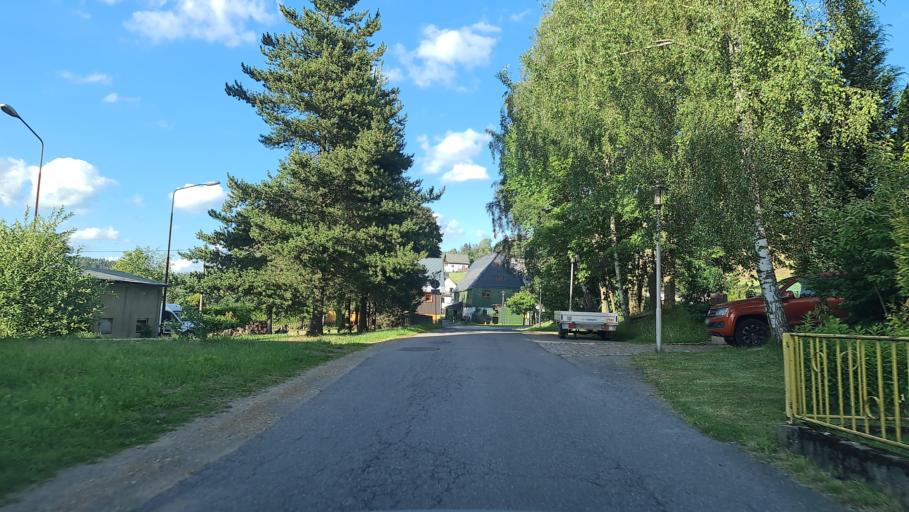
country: DE
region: Saxony
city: Neuhausen
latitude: 50.6807
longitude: 13.4745
